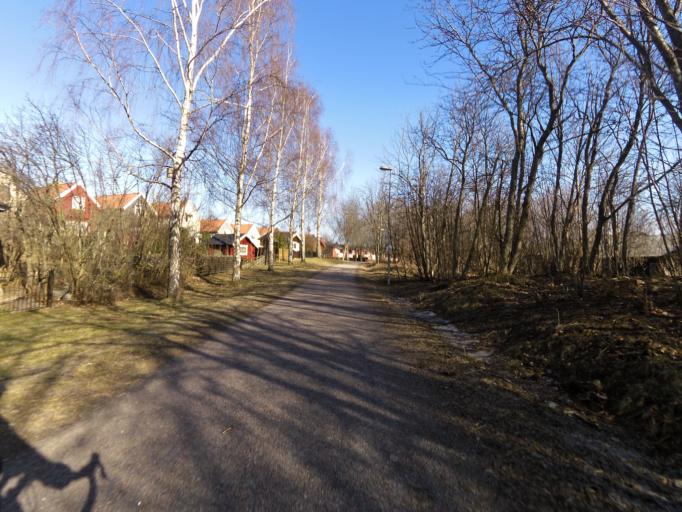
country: SE
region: Gaevleborg
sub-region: Gavle Kommun
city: Gavle
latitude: 60.6697
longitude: 17.1742
